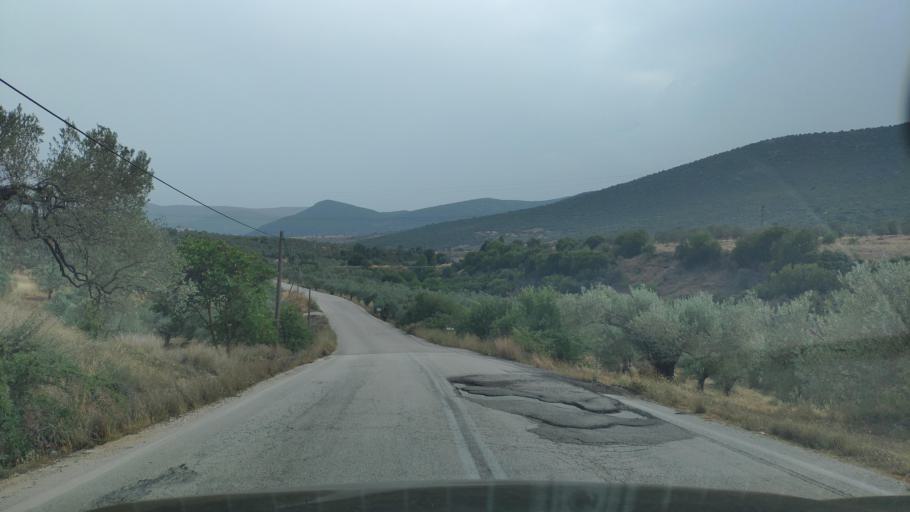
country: GR
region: Peloponnese
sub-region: Nomos Argolidos
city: Palaia Epidavros
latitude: 37.5741
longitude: 23.1499
